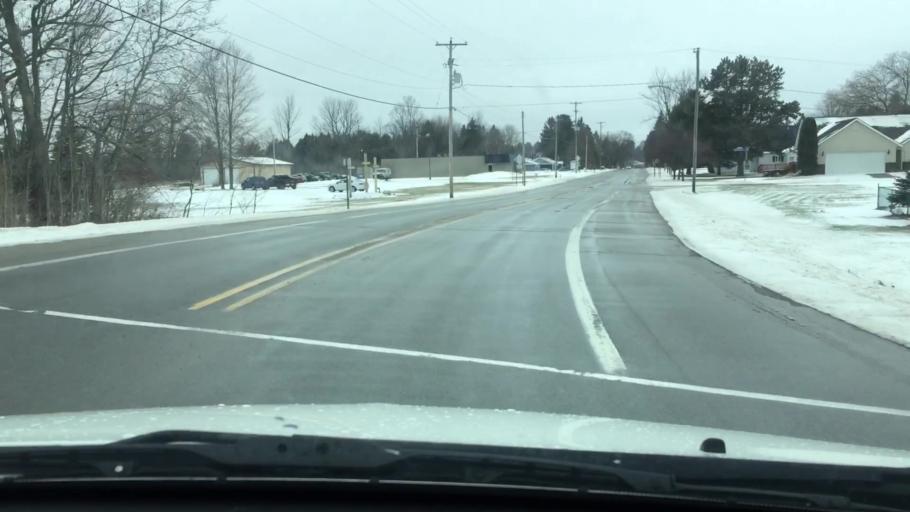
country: US
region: Michigan
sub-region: Wexford County
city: Cadillac
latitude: 44.2339
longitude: -85.4148
